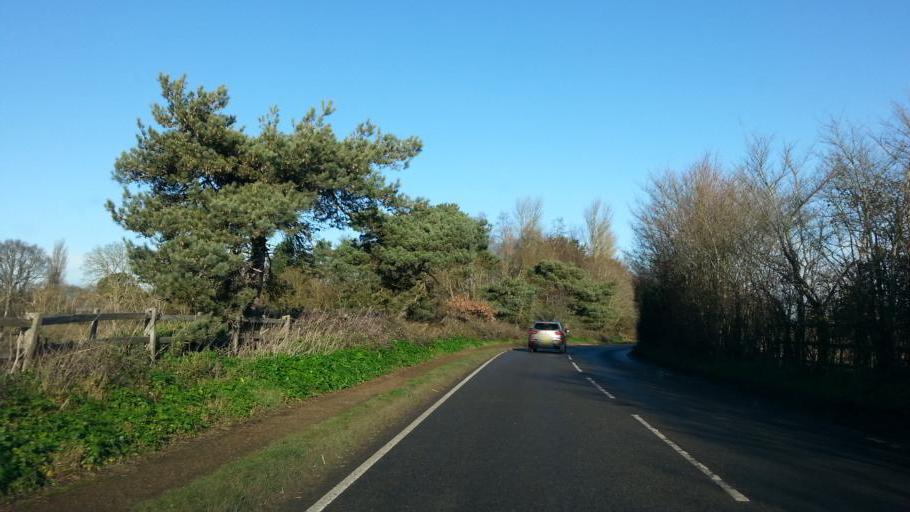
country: GB
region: England
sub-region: Suffolk
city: Saxmundham
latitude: 52.1763
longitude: 1.5015
